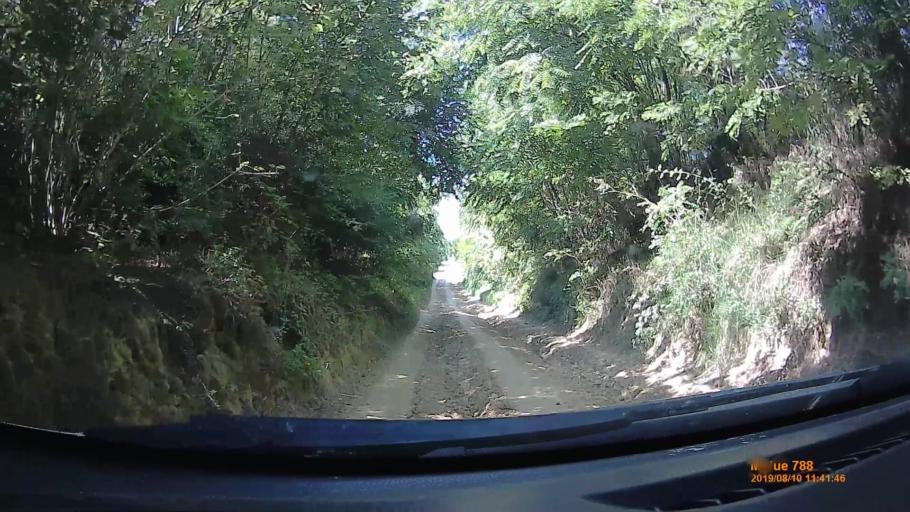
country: HU
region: Somogy
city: Somogyvar
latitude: 46.5147
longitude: 17.7643
